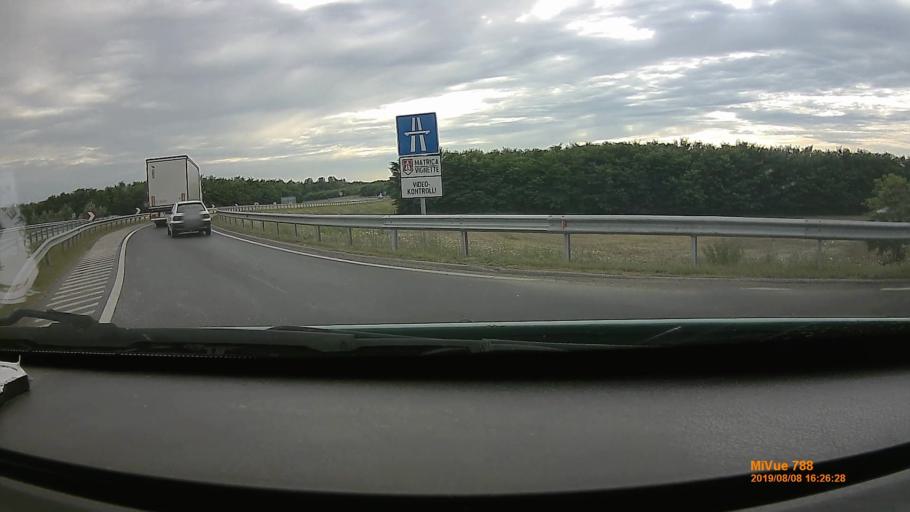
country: HU
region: Szabolcs-Szatmar-Bereg
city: Vaja
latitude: 47.9721
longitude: 22.2033
